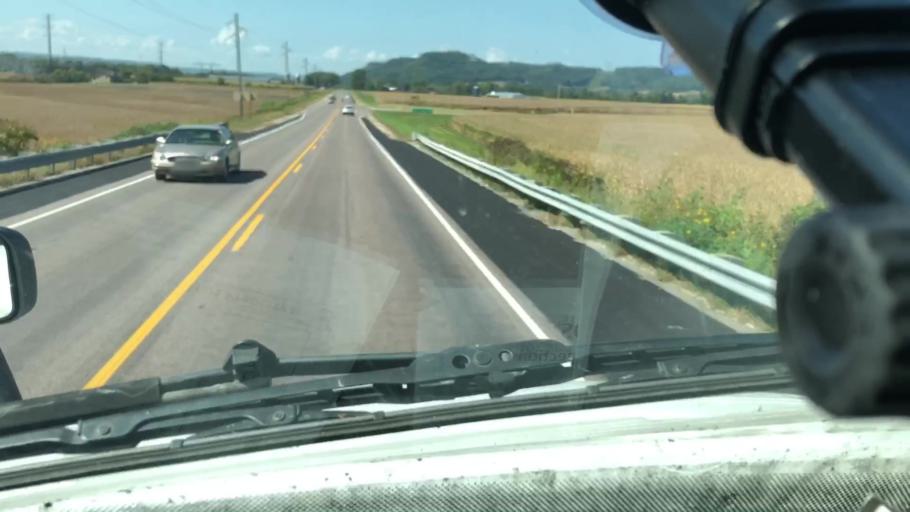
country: US
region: Wisconsin
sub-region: Trempealeau County
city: Trempealeau
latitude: 44.0699
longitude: -91.5200
